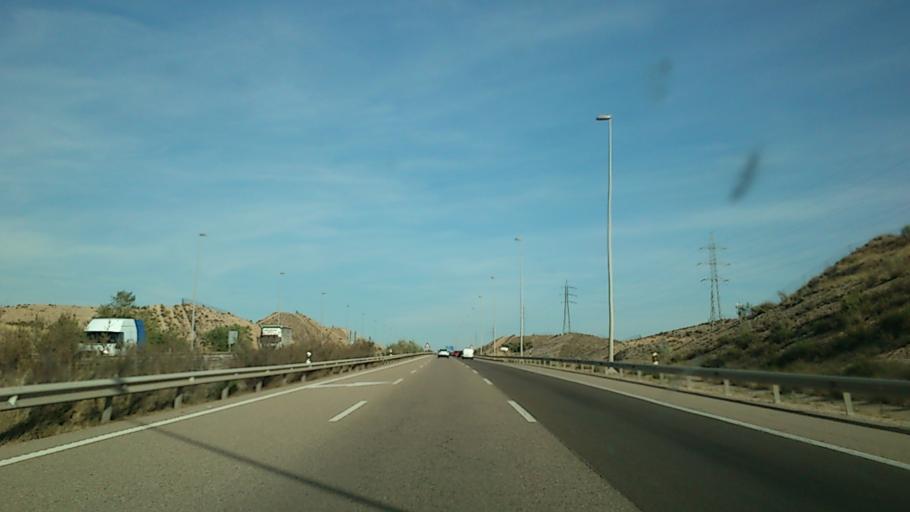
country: ES
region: Aragon
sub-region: Provincia de Zaragoza
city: Cuarte de Huerva
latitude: 41.6081
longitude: -0.9135
